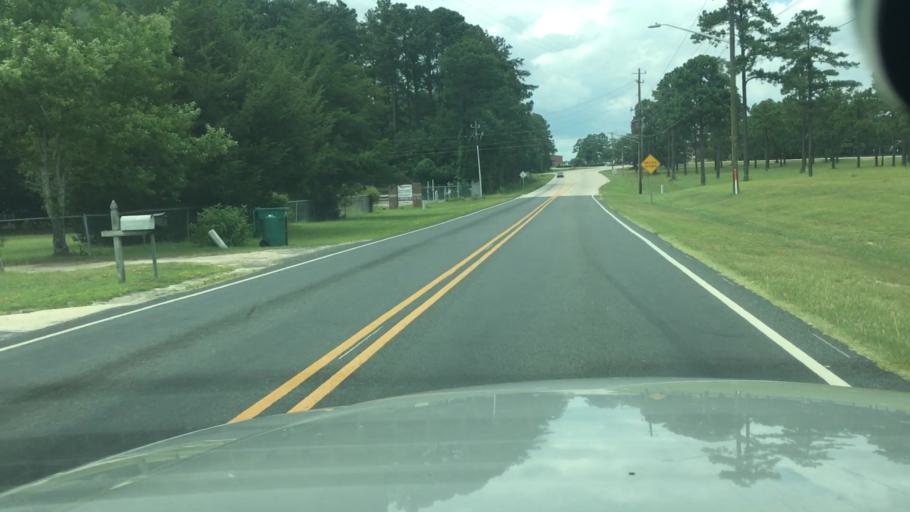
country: US
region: North Carolina
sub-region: Cumberland County
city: Hope Mills
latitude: 34.9930
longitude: -78.8912
